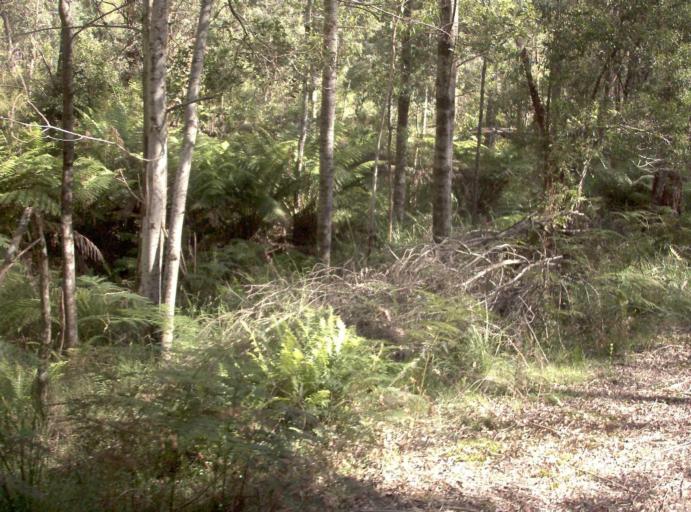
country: AU
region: Victoria
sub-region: East Gippsland
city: Lakes Entrance
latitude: -37.3924
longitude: 148.5965
